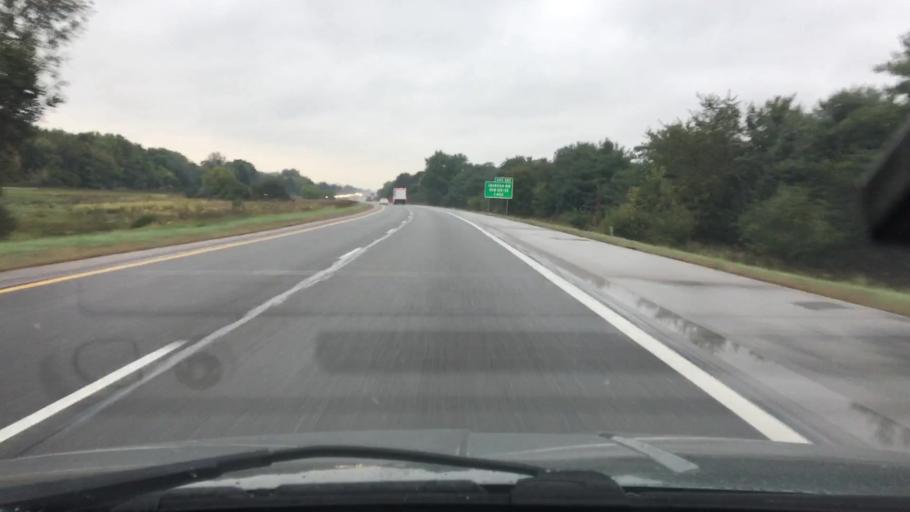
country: US
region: Michigan
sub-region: Washtenaw County
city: Chelsea
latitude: 42.2998
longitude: -83.9510
